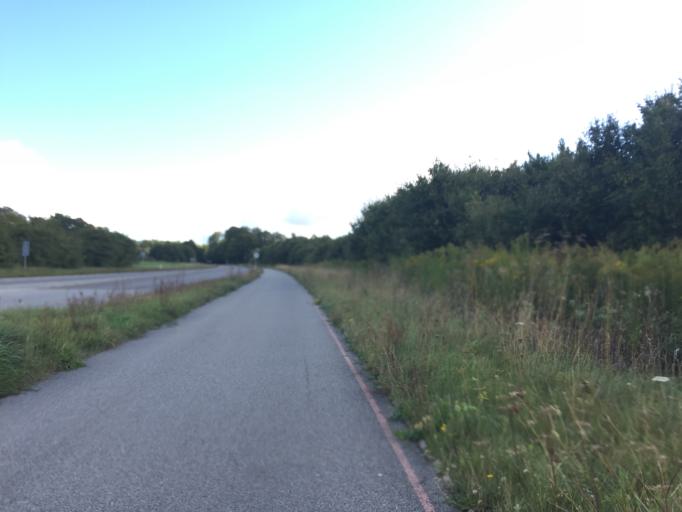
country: DK
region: Capital Region
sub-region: Fureso Kommune
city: Stavnsholt
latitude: 55.7781
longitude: 12.4056
